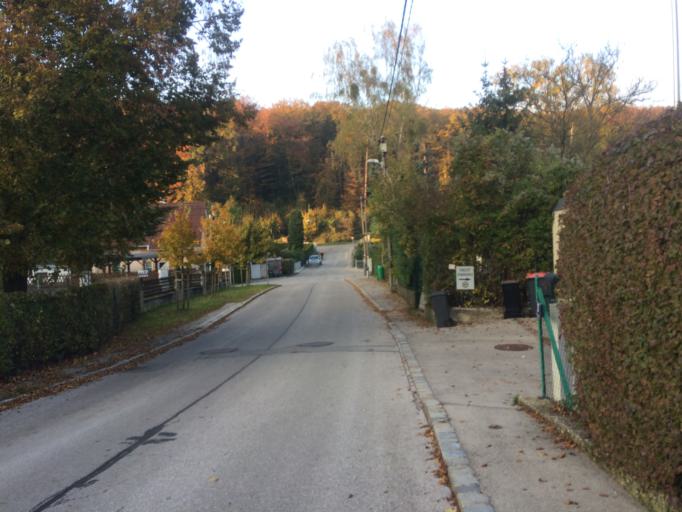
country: AT
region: Lower Austria
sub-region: Politischer Bezirk Wien-Umgebung
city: Gablitz
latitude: 48.2222
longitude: 16.1369
